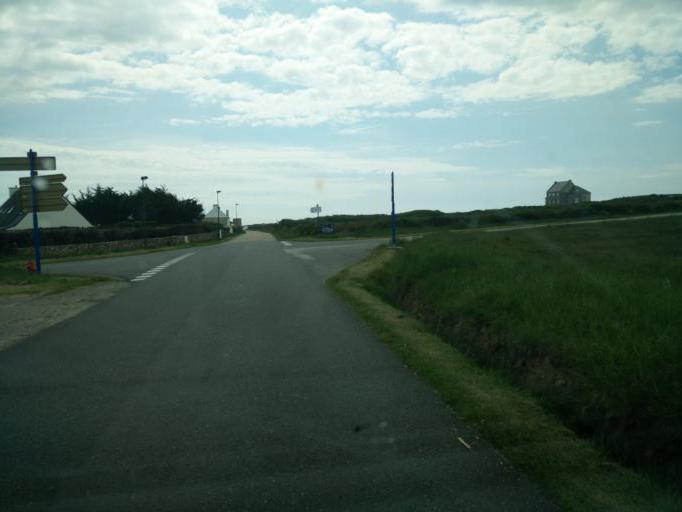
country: FR
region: Brittany
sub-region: Departement du Finistere
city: Camaret-sur-Mer
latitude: 48.2723
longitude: -4.6100
